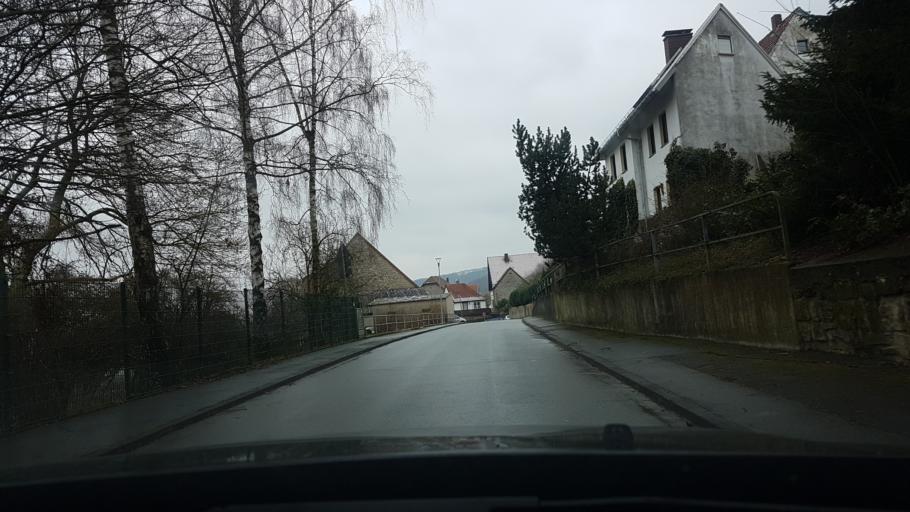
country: DE
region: North Rhine-Westphalia
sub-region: Regierungsbezirk Detmold
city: Willebadessen
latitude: 51.5306
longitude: 9.0259
